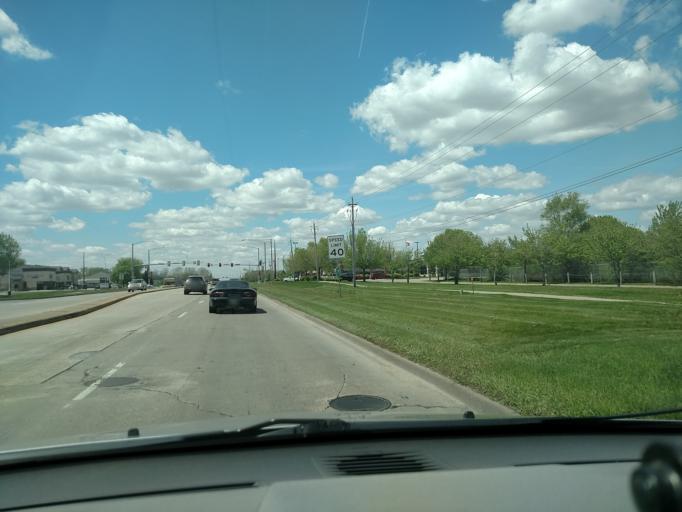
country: US
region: Iowa
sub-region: Polk County
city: Ankeny
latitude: 41.7029
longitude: -93.5824
